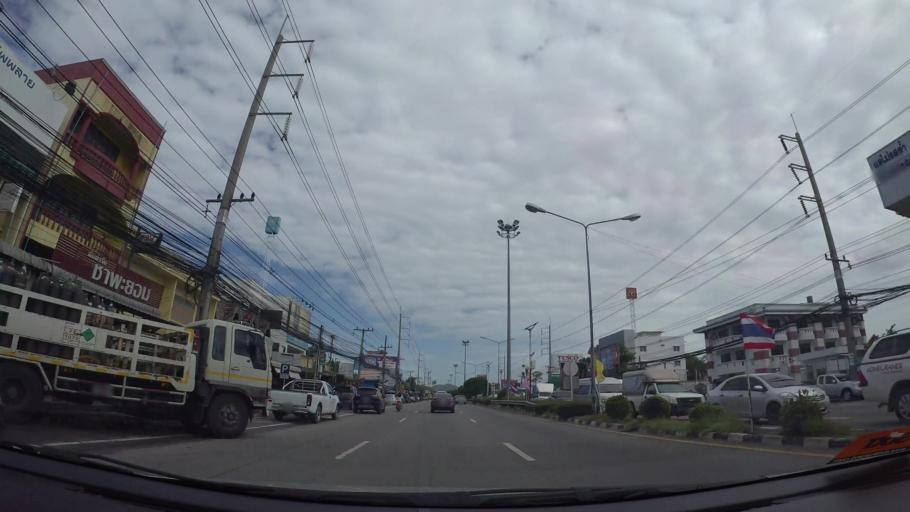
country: TH
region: Rayong
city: Rayong
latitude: 12.7147
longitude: 101.1660
